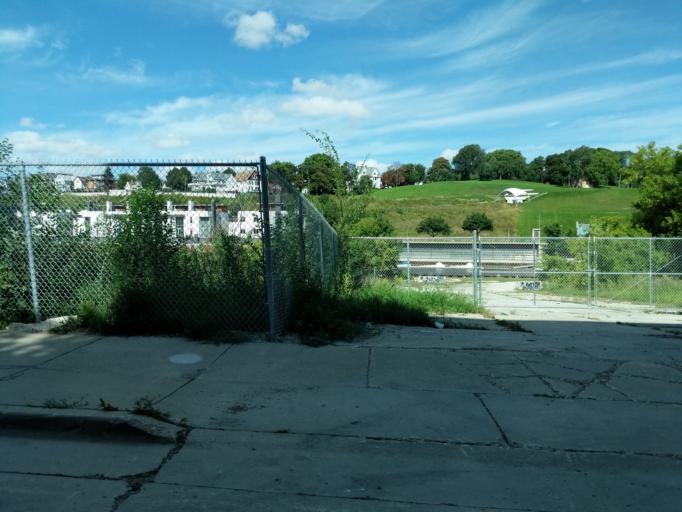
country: US
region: Wisconsin
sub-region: Milwaukee County
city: Milwaukee
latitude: 43.0557
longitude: -87.9007
